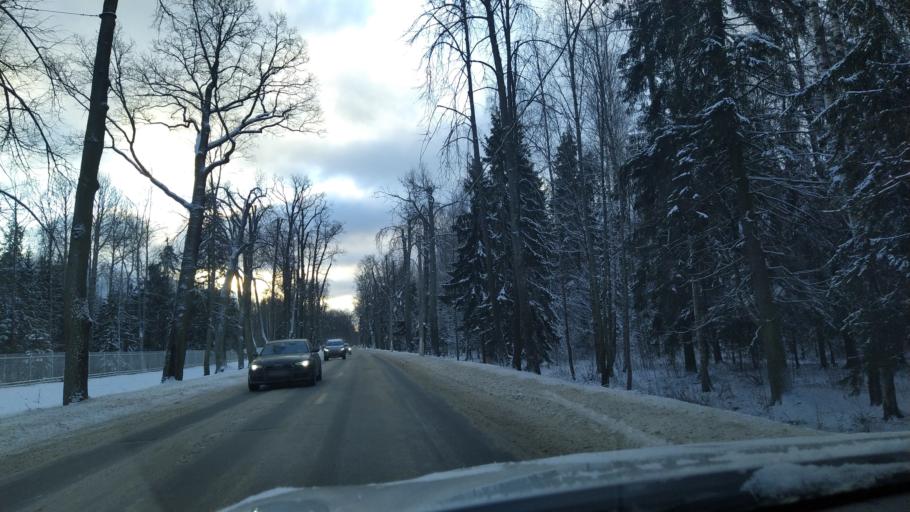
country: RU
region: St.-Petersburg
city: Aleksandrovskaya
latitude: 59.7240
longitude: 30.3614
